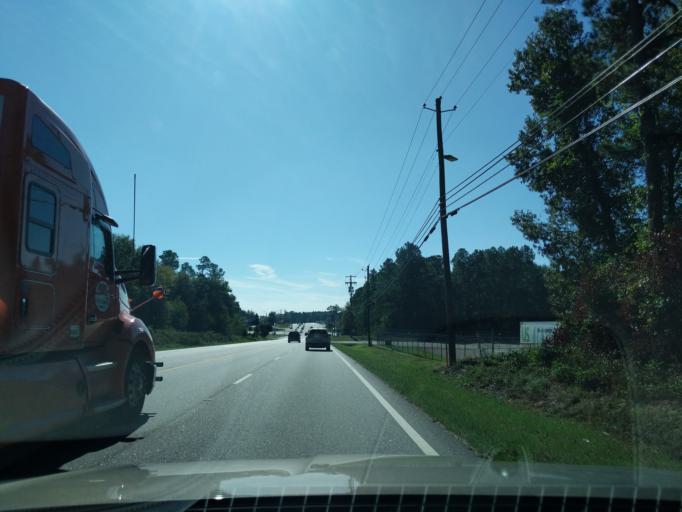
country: US
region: Georgia
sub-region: Richmond County
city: Augusta
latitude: 33.3720
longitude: -81.9985
